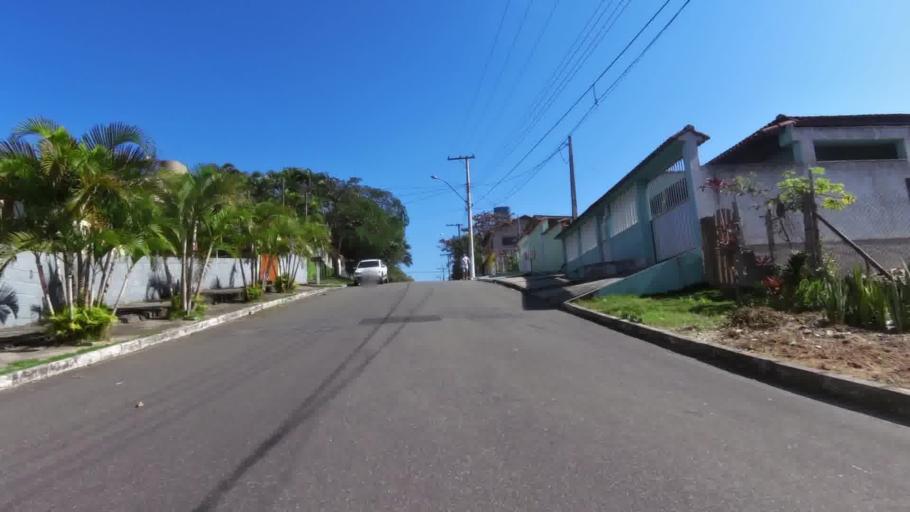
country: BR
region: Espirito Santo
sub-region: Guarapari
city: Guarapari
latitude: -20.7357
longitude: -40.5425
